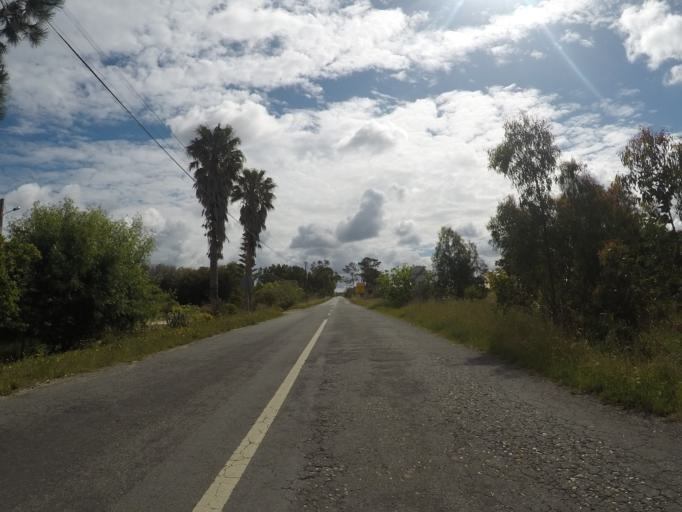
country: PT
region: Beja
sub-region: Odemira
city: Sao Teotonio
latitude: 37.4803
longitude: -8.7733
